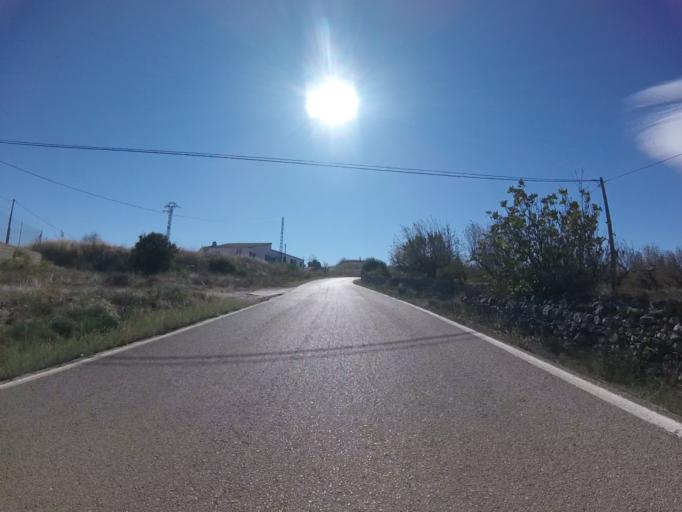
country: ES
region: Valencia
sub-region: Provincia de Castello
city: Albocasser
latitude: 40.3692
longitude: 0.0198
